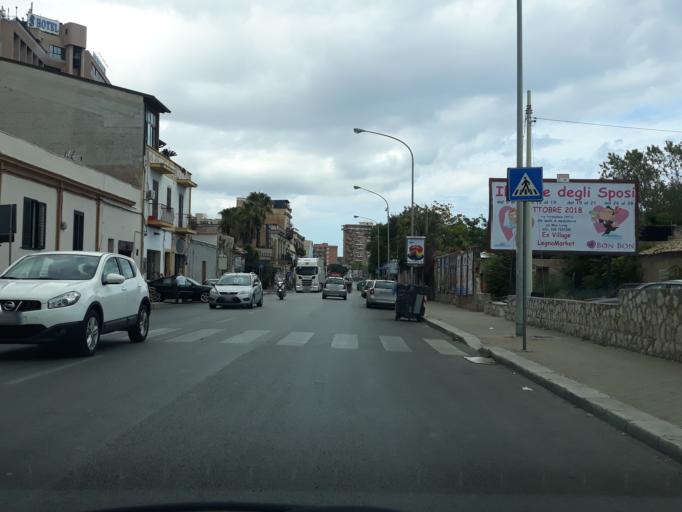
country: IT
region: Sicily
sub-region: Palermo
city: Ciaculli
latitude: 38.1072
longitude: 13.3825
